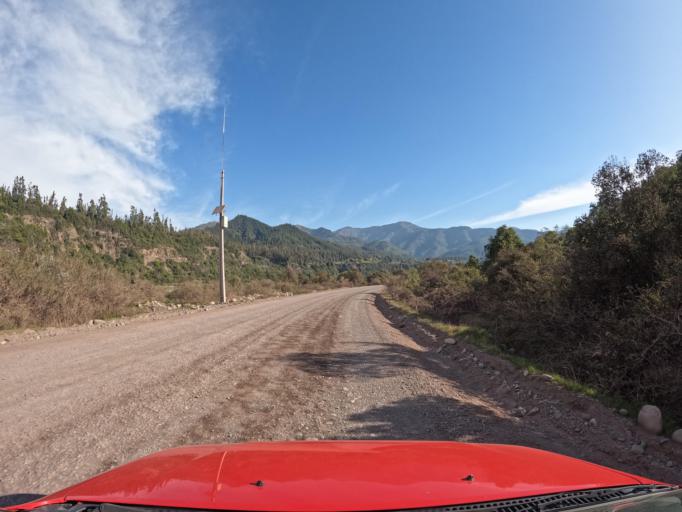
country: CL
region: Maule
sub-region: Provincia de Curico
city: Teno
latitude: -35.0003
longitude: -70.8267
